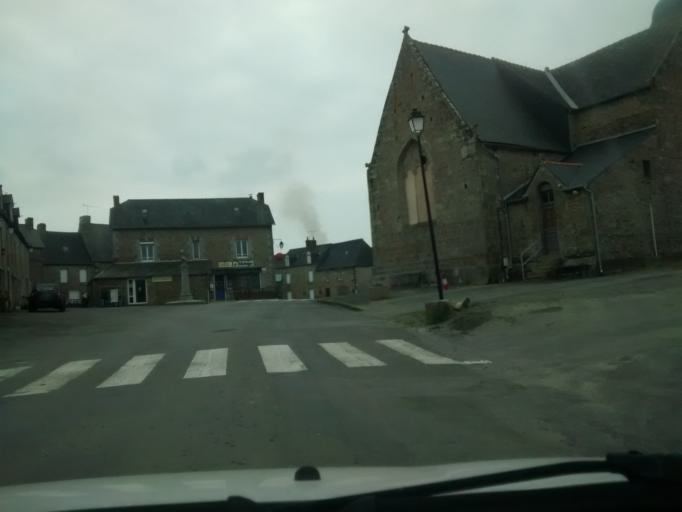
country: FR
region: Brittany
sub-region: Departement d'Ille-et-Vilaine
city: Tremblay
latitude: 48.3991
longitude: -1.5120
